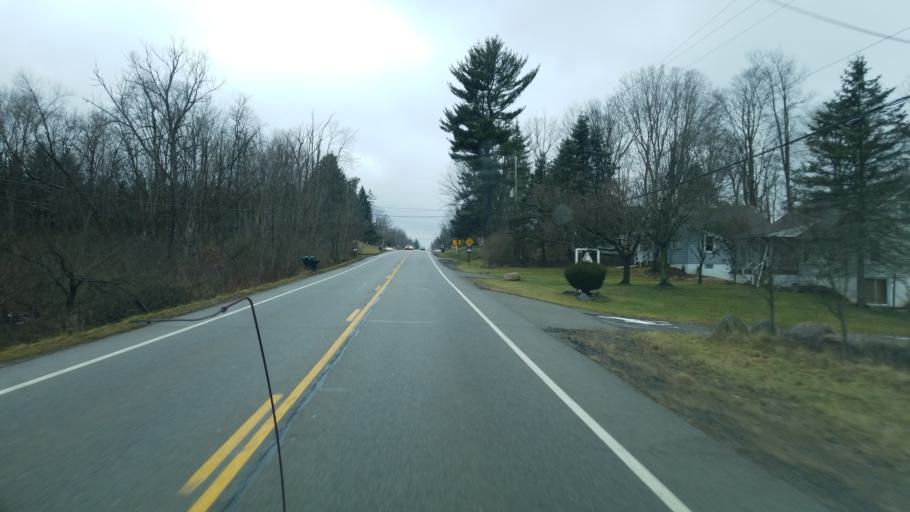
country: US
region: Ohio
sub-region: Portage County
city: Streetsboro
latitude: 41.2399
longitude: -81.3847
